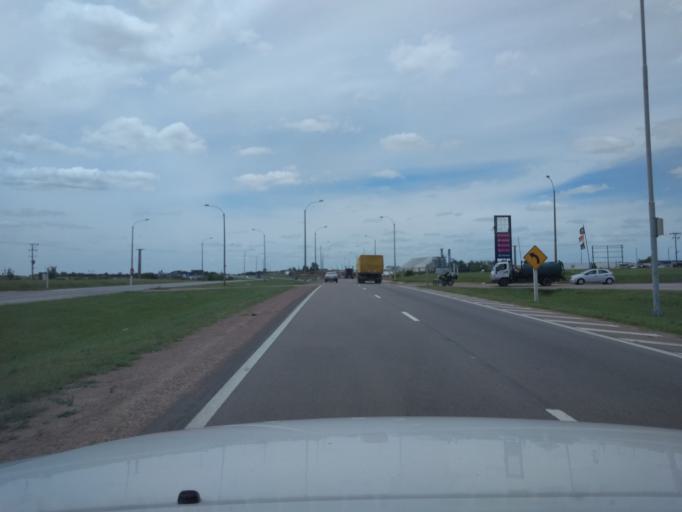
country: UY
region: Canelones
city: La Paz
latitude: -34.7507
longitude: -56.2554
